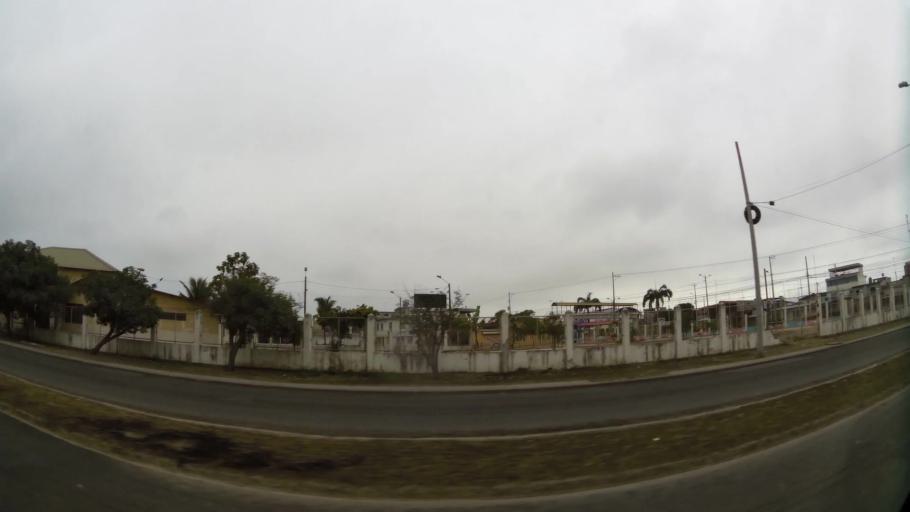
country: EC
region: El Oro
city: Machala
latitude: -3.2526
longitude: -79.9759
